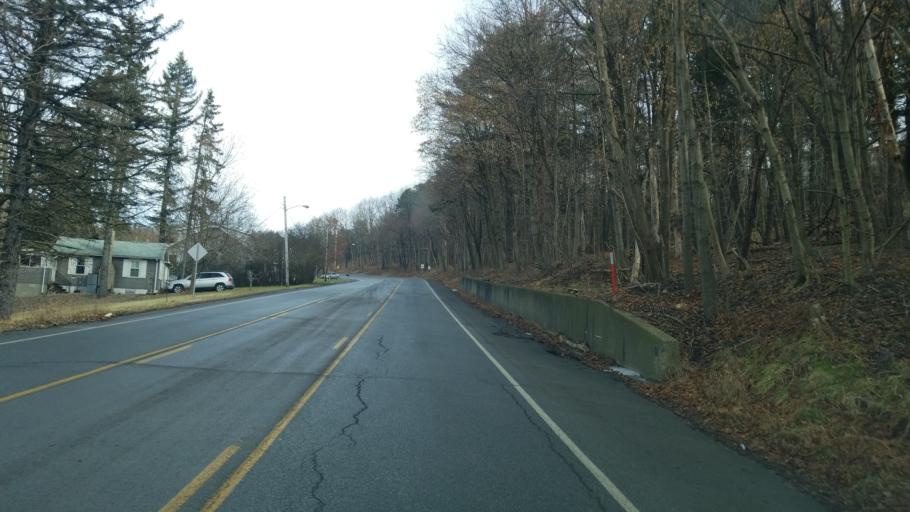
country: US
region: Pennsylvania
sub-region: Indiana County
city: Chevy Chase Heights
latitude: 40.6318
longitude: -79.1429
